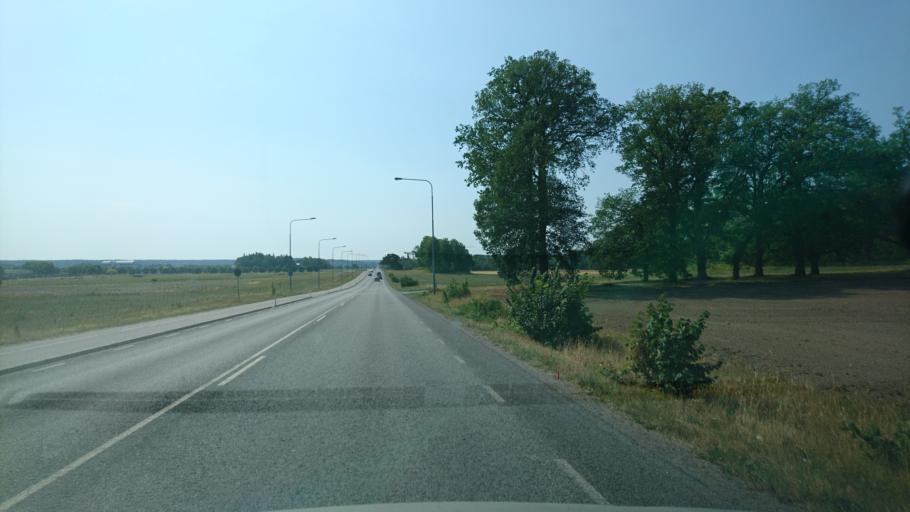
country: SE
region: Uppsala
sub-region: Uppsala Kommun
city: Uppsala
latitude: 59.8241
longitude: 17.6456
